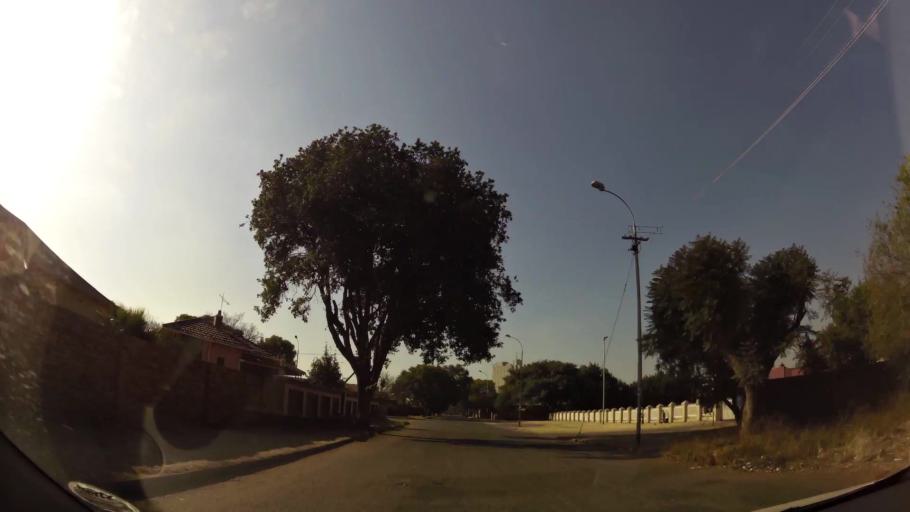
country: ZA
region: Gauteng
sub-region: West Rand District Municipality
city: Randfontein
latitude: -26.1705
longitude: 27.7090
